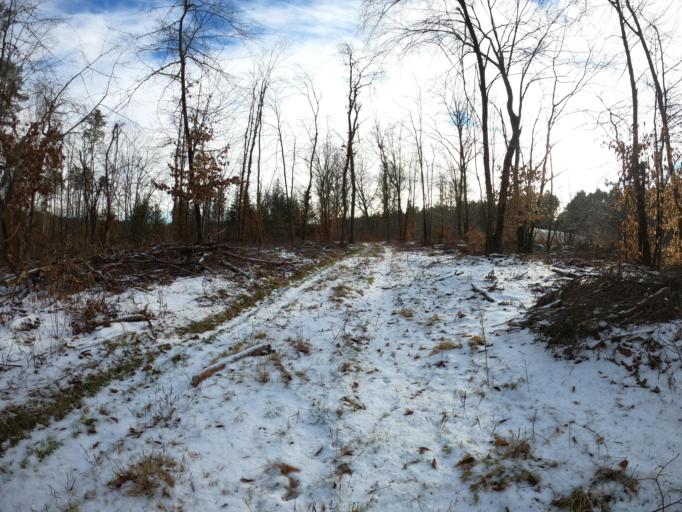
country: PL
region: Lubusz
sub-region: Powiat slubicki
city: Rzepin
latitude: 52.2943
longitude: 14.8162
